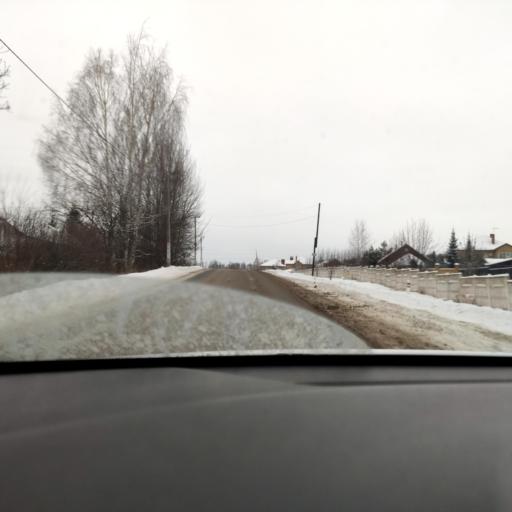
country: RU
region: Tatarstan
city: Osinovo
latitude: 55.8564
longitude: 48.8209
